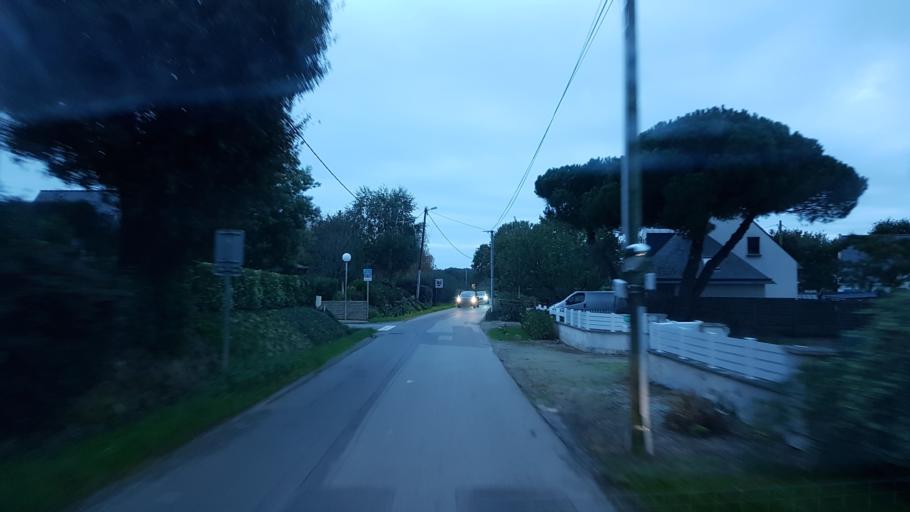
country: FR
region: Brittany
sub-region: Departement du Morbihan
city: Sarzeau
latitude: 47.5395
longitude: -2.7939
